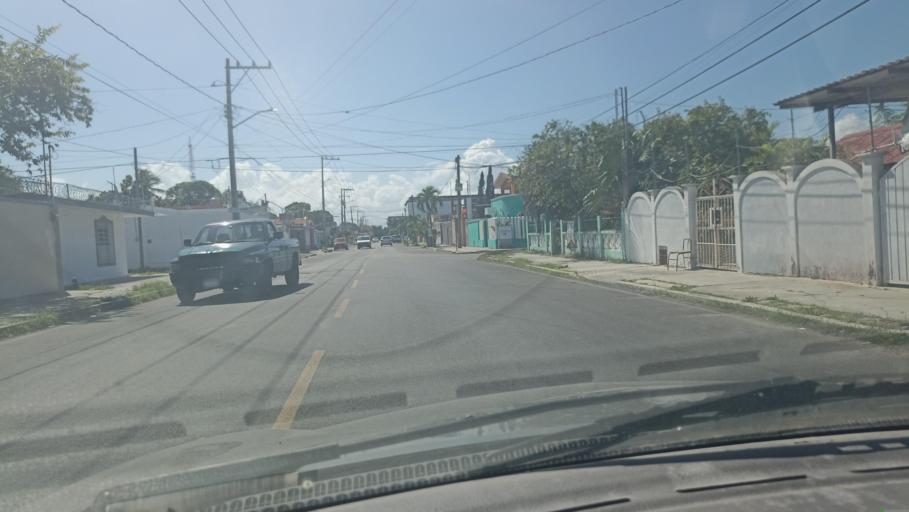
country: MX
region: Quintana Roo
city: Chetumal
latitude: 18.5103
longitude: -88.2904
